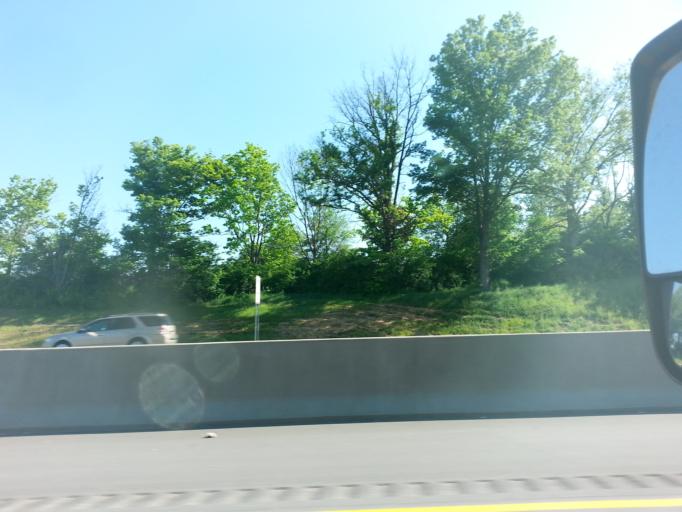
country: US
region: Kentucky
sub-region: Shelby County
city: Shelbyville
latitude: 38.1957
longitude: -85.2838
